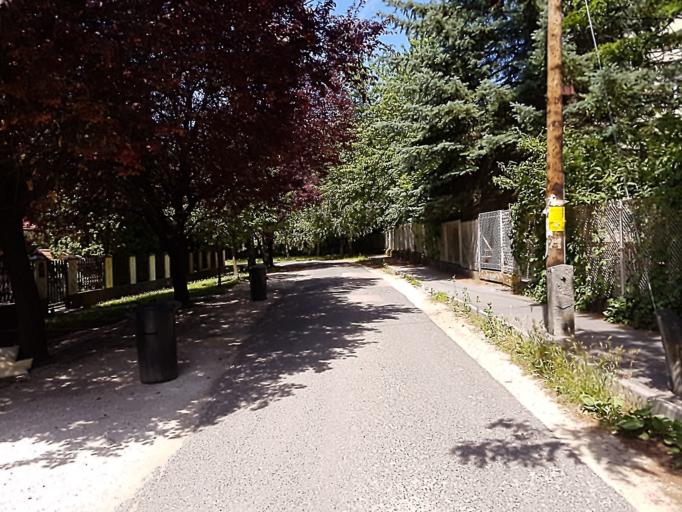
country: HU
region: Pest
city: Solymar
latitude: 47.5601
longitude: 18.9446
